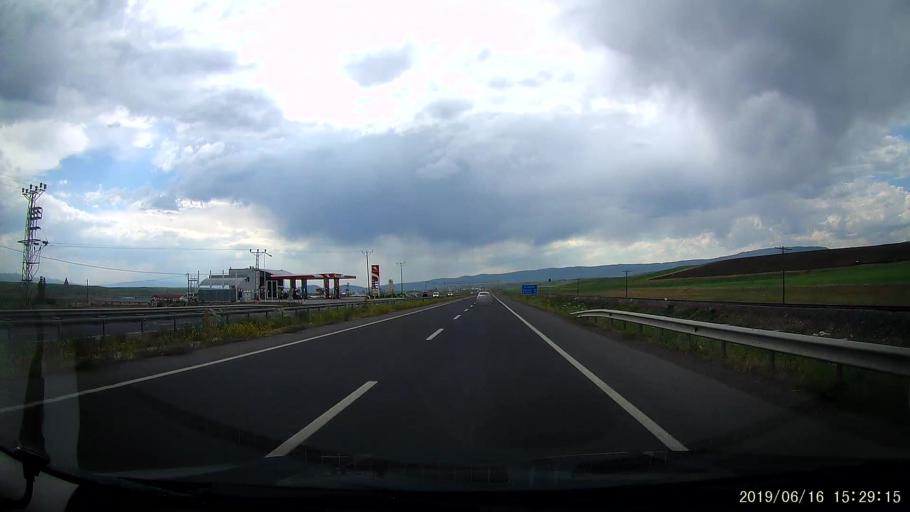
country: TR
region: Erzurum
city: Horasan
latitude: 40.0316
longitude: 42.1365
